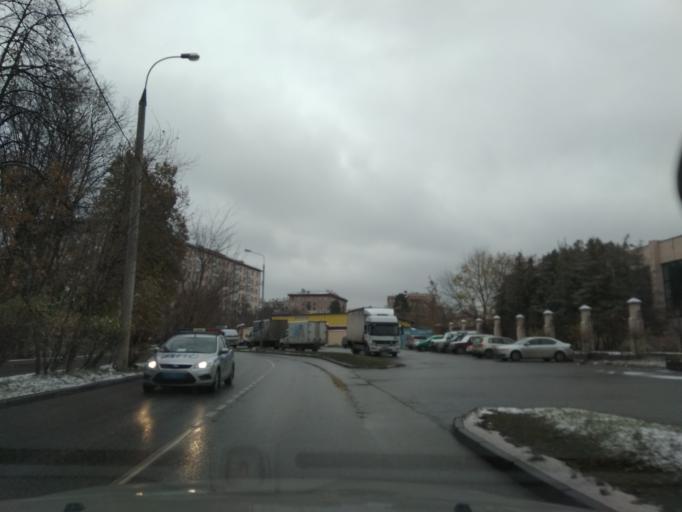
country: RU
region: Moscow
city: Pokrovskoye-Streshnevo
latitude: 55.8000
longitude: 37.4705
